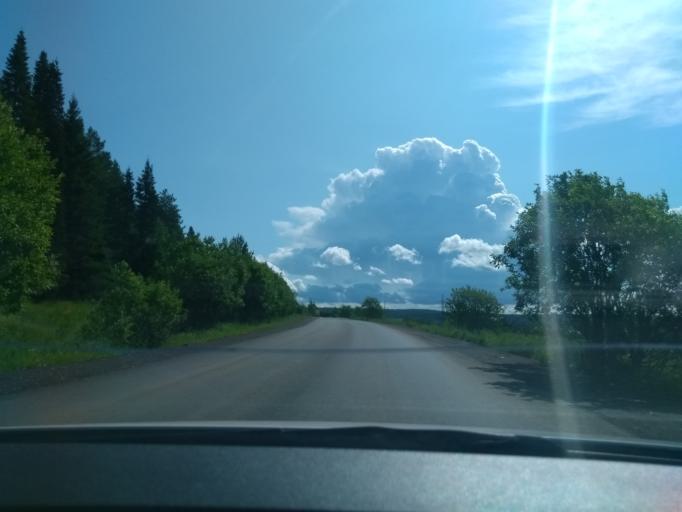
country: RU
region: Perm
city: Kukushtan
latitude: 57.8142
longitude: 56.5497
